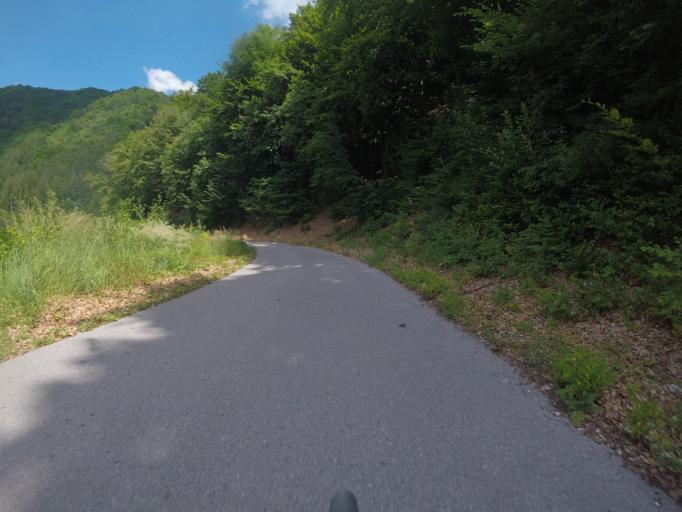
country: SI
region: Kostanjevica na Krki
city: Kostanjevica na Krki
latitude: 45.7702
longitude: 15.4169
